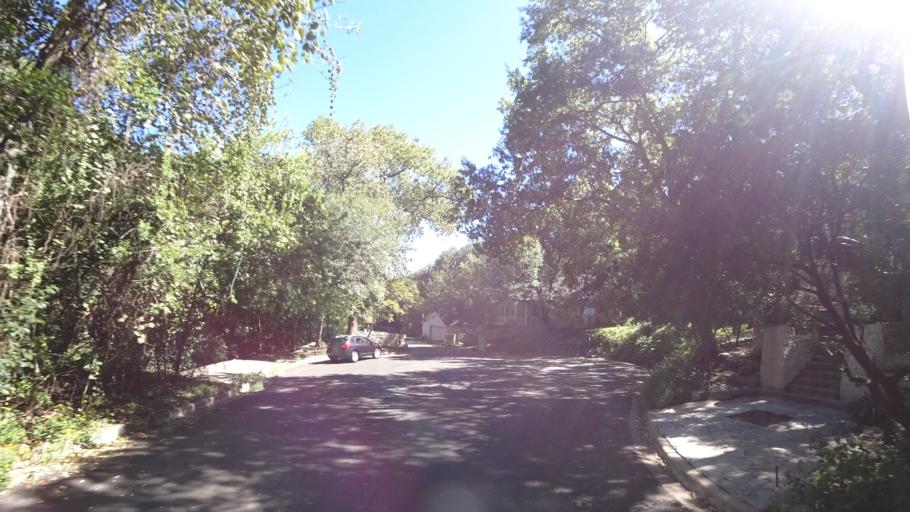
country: US
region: Texas
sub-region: Travis County
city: West Lake Hills
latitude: 30.3267
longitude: -97.7707
